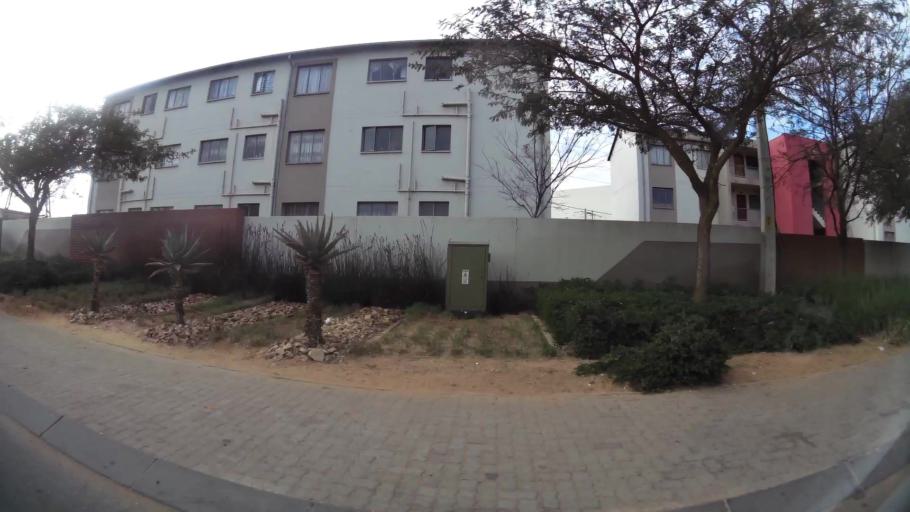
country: ZA
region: Gauteng
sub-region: City of Johannesburg Metropolitan Municipality
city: Roodepoort
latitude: -26.1890
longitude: 27.9101
